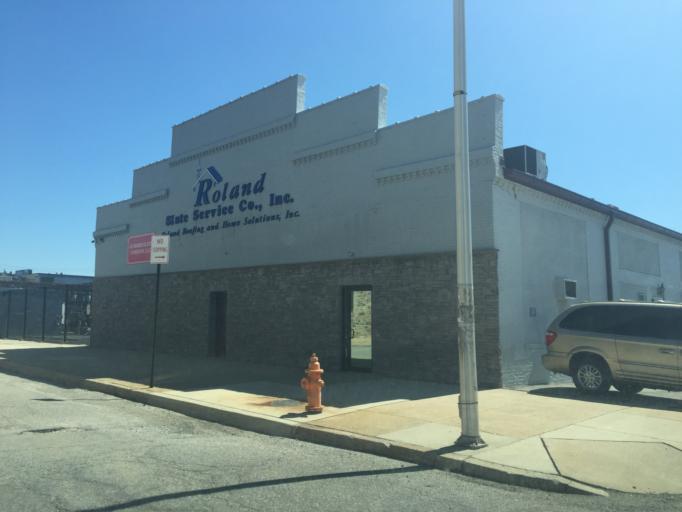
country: US
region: Maryland
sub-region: City of Baltimore
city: Baltimore
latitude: 39.3151
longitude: -76.6219
